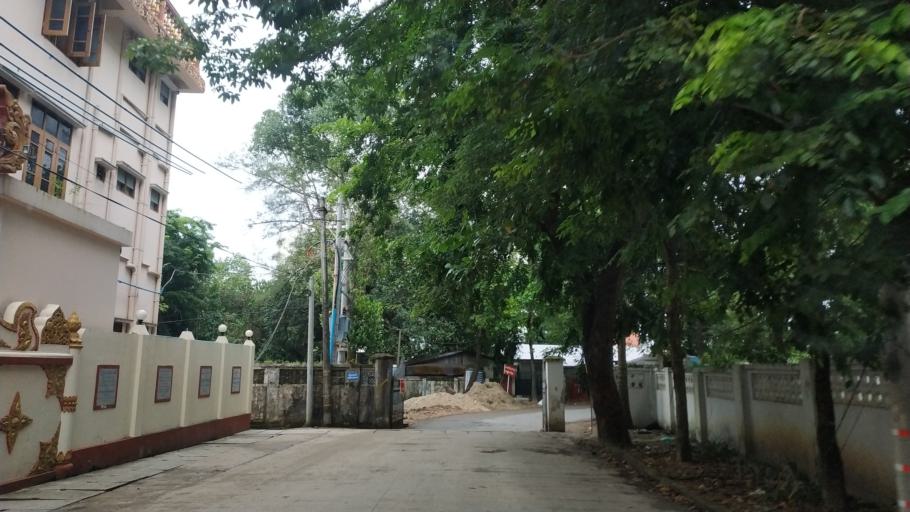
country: MM
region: Yangon
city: Yangon
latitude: 16.8479
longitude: 96.1336
